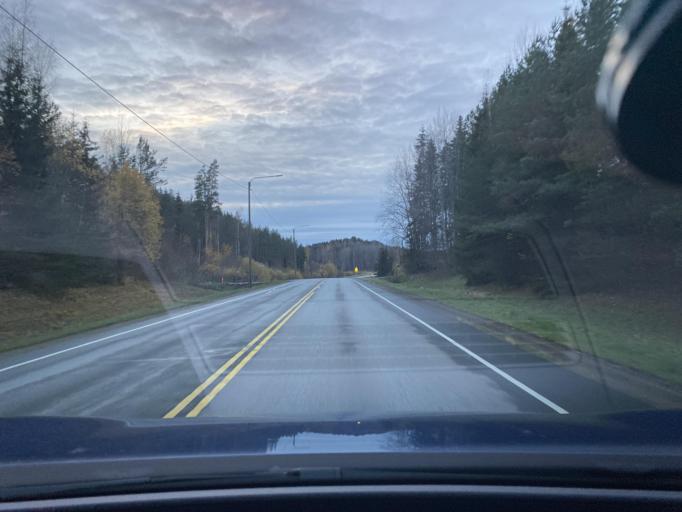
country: FI
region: Uusimaa
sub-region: Helsinki
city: Saukkola
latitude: 60.3852
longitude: 24.0715
